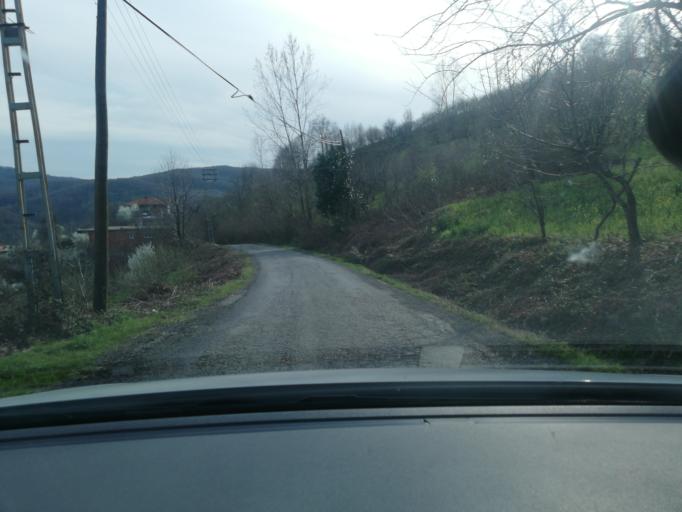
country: TR
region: Zonguldak
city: Kozlu
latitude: 41.3568
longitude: 31.6448
